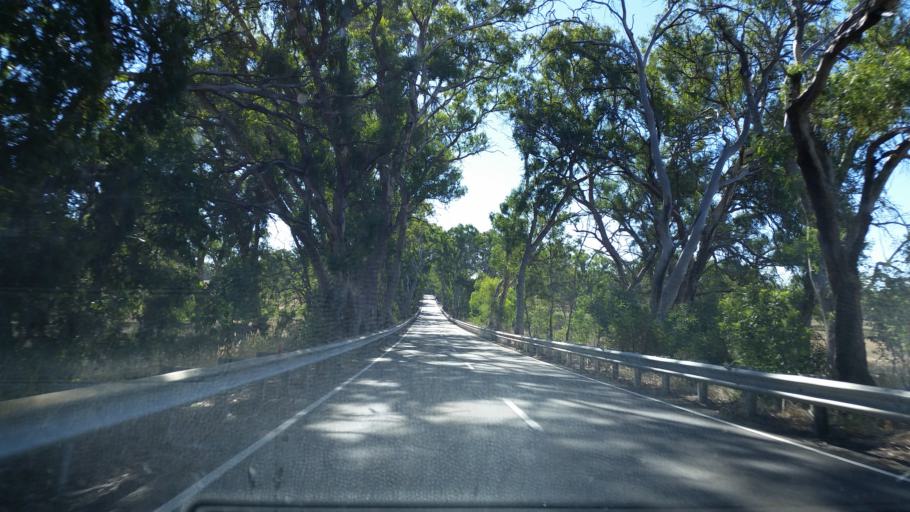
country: AU
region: South Australia
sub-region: Adelaide Hills
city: Birdwood
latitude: -34.8141
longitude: 139.0389
